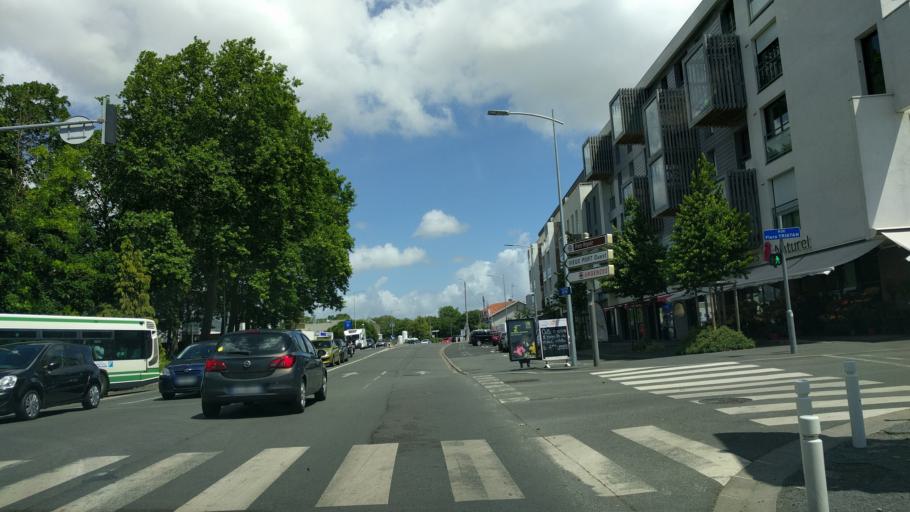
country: FR
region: Poitou-Charentes
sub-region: Departement de la Charente-Maritime
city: La Rochelle
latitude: 46.1578
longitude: -1.1423
